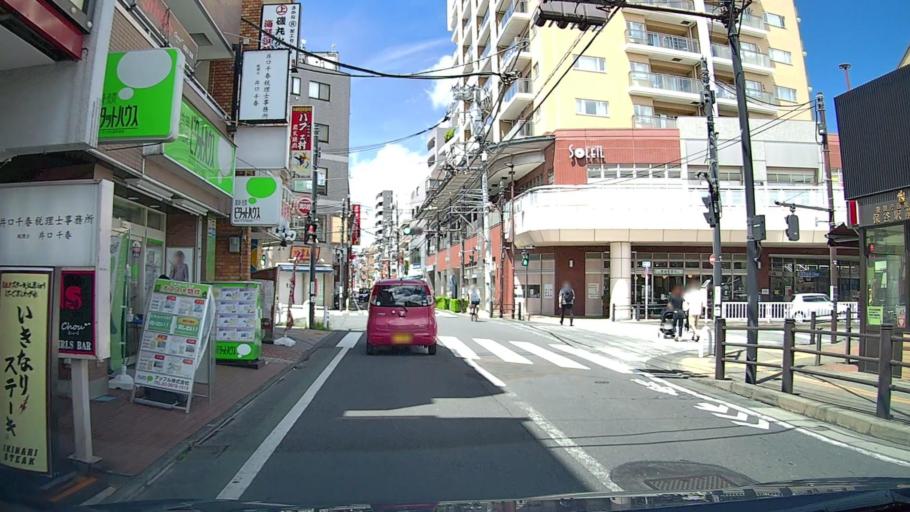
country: JP
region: Tokyo
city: Nishi-Tokyo-shi
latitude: 35.7478
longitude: 139.5670
